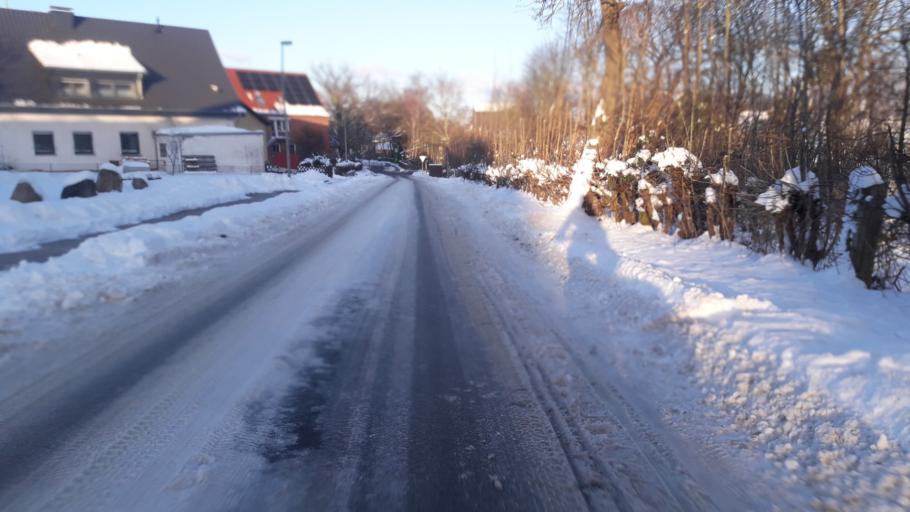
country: DE
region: North Rhine-Westphalia
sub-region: Regierungsbezirk Detmold
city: Salzkotten
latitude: 51.6307
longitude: 8.6776
